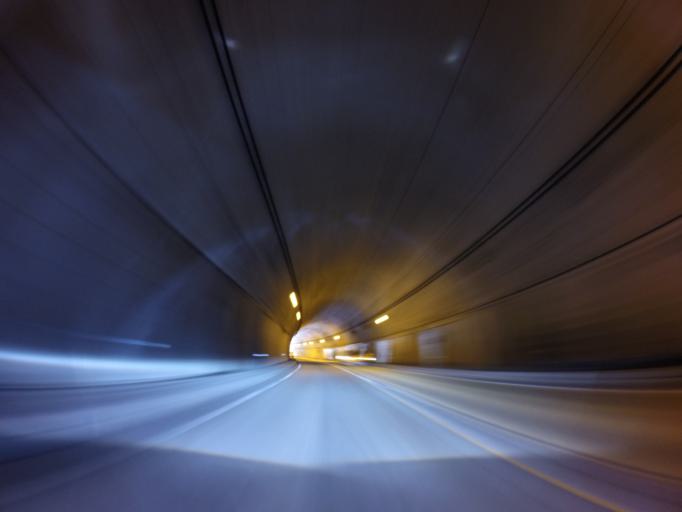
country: JP
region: Shizuoka
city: Shimoda
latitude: 34.8116
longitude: 138.9291
